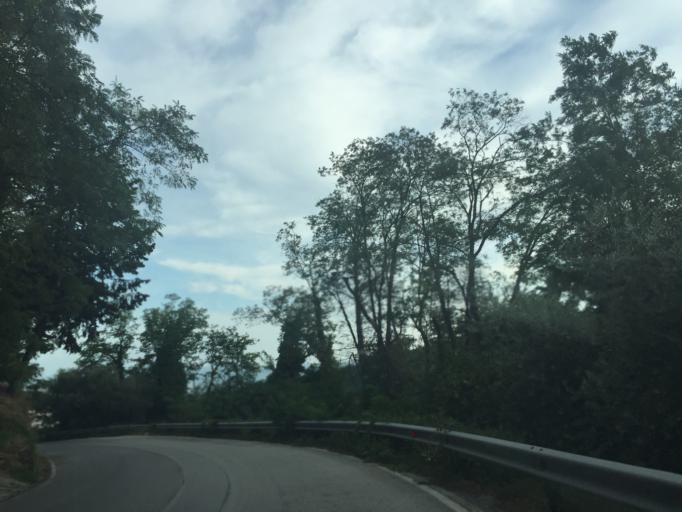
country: IT
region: Tuscany
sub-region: Provincia di Pistoia
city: Campo Tizzoro
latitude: 43.9811
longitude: 10.8634
